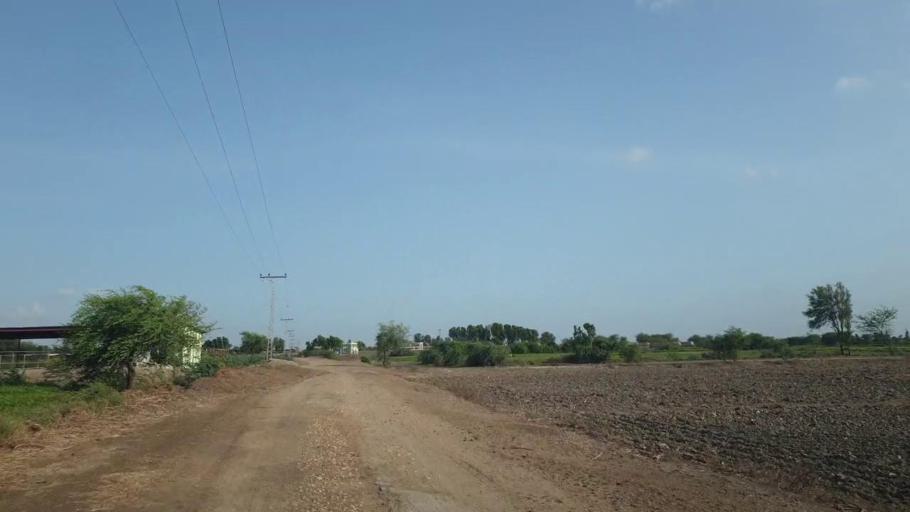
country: PK
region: Sindh
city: Kadhan
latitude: 24.6250
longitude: 69.0847
